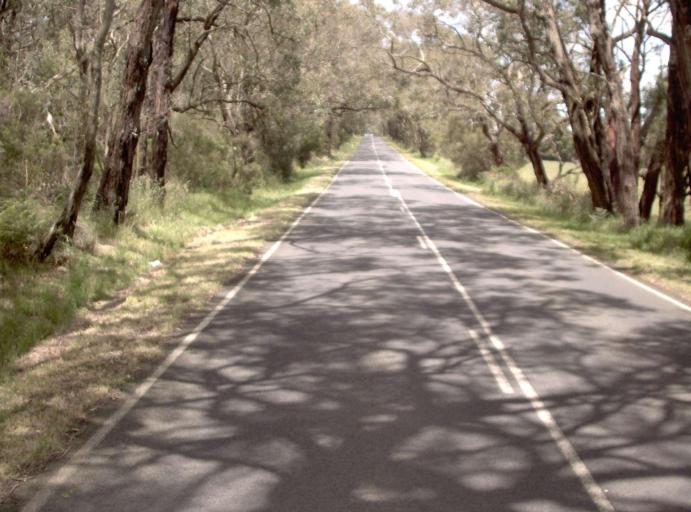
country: AU
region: Victoria
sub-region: Bass Coast
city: North Wonthaggi
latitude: -38.6196
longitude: 146.0152
